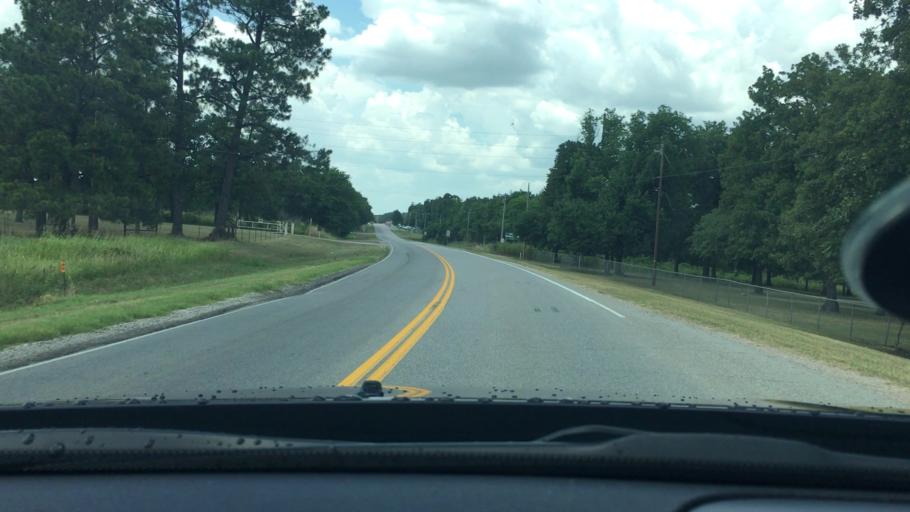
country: US
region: Oklahoma
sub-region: Johnston County
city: Tishomingo
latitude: 34.2293
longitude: -96.6973
